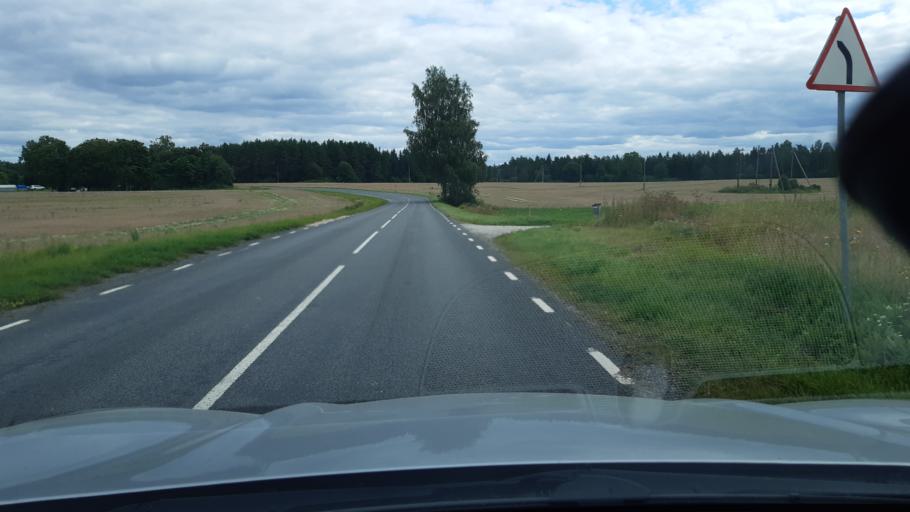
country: EE
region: Raplamaa
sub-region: Maerjamaa vald
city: Marjamaa
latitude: 59.0399
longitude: 24.4931
